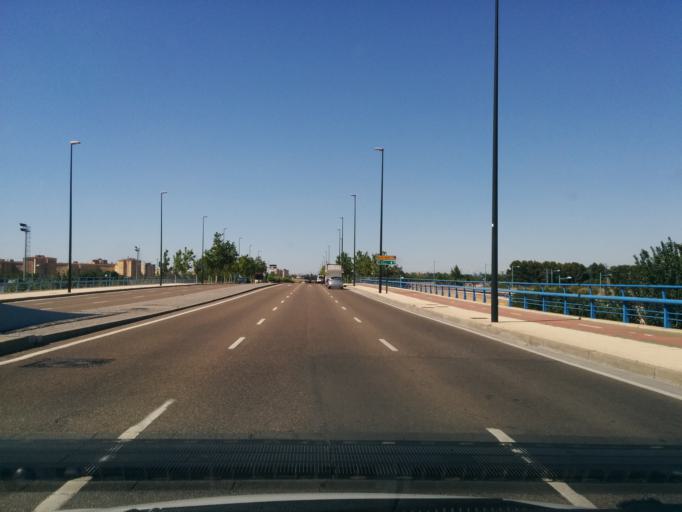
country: ES
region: Aragon
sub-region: Provincia de Zaragoza
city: Zaragoza
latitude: 41.6514
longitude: -0.8545
